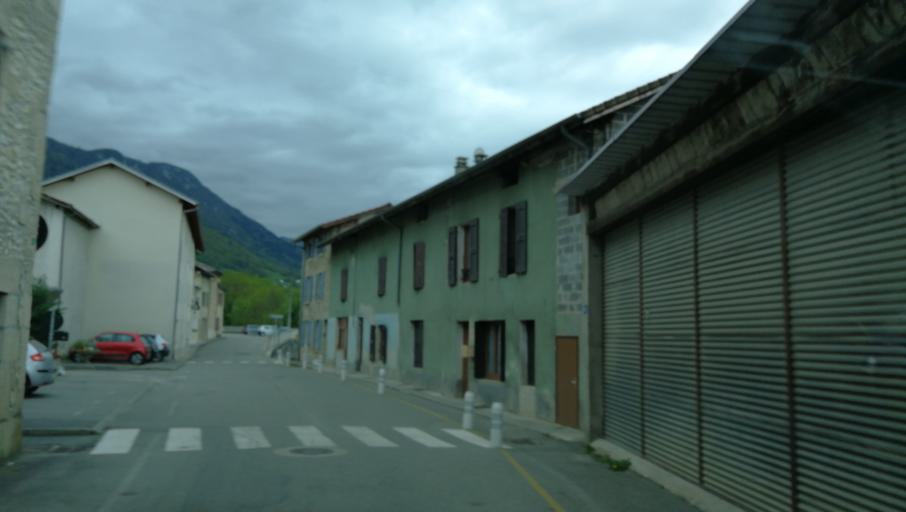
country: FR
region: Rhone-Alpes
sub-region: Departement de la Drome
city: Saint-Jean-en-Royans
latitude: 45.0154
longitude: 5.2883
